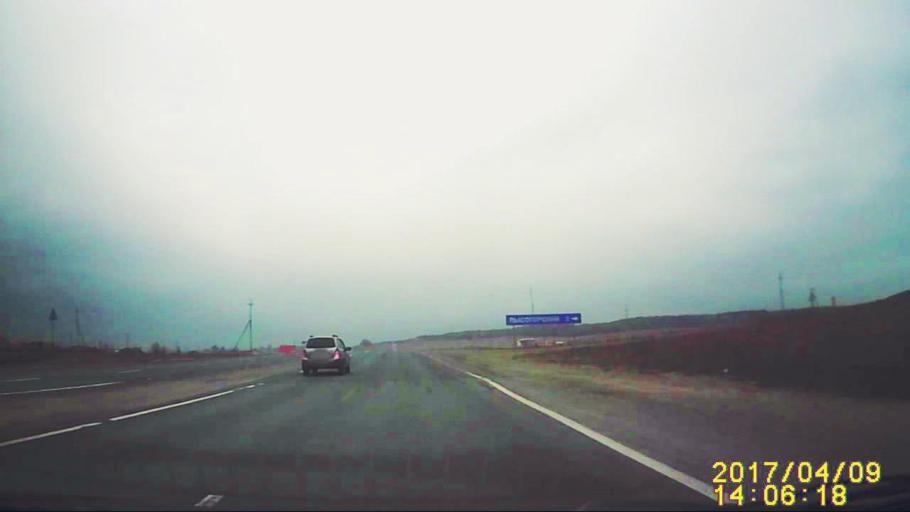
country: RU
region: Ulyanovsk
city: Silikatnyy
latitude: 54.0019
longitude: 48.2211
